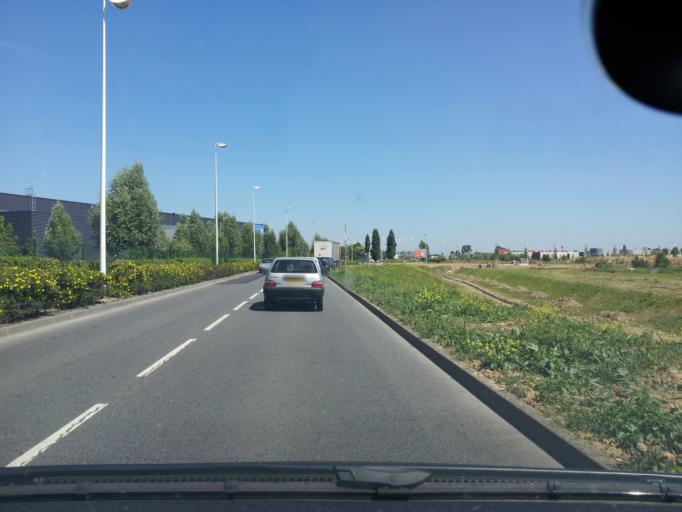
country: FR
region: Ile-de-France
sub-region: Departement de l'Essonne
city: Marolles-en-Hurepoix
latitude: 48.5801
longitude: 2.2990
